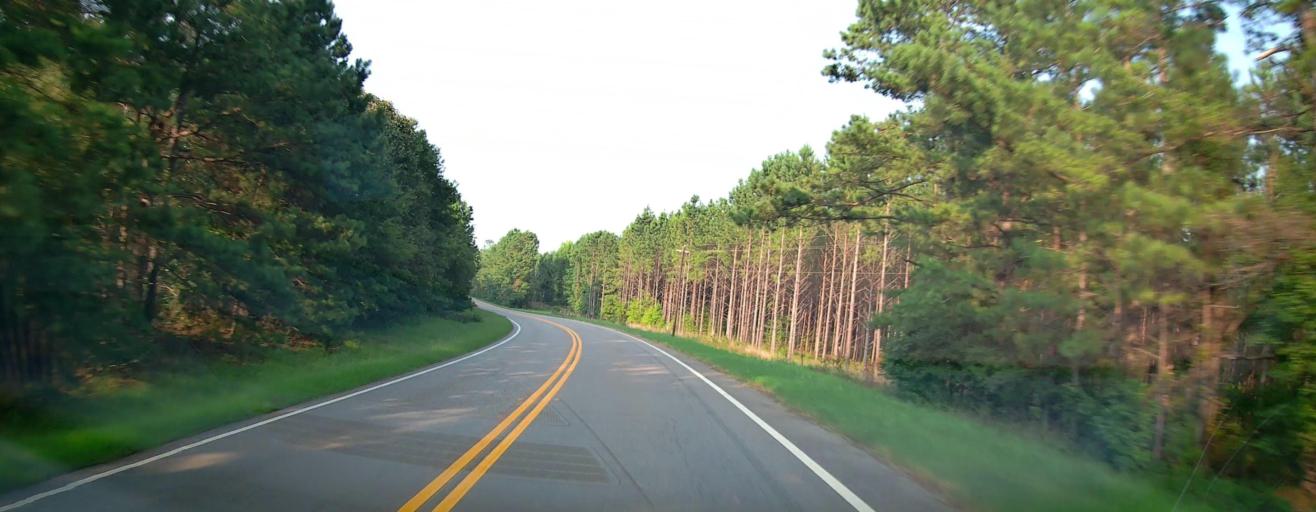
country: US
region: Georgia
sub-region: Jones County
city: Gray
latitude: 33.0600
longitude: -83.5890
